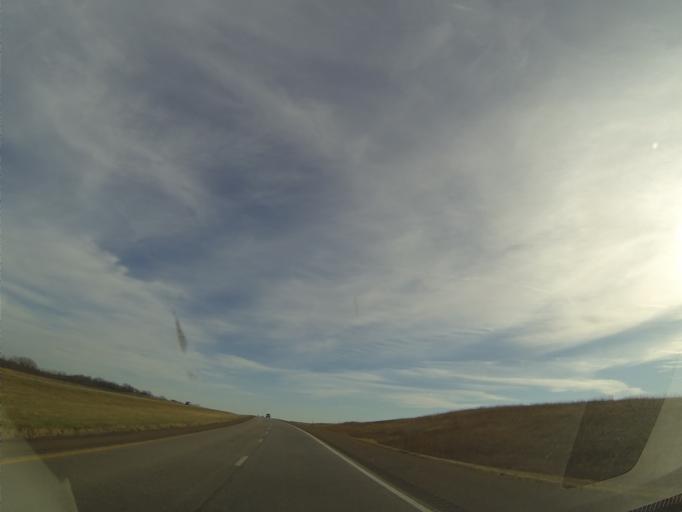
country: US
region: Kansas
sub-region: Ottawa County
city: Minneapolis
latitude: 39.0415
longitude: -97.6499
